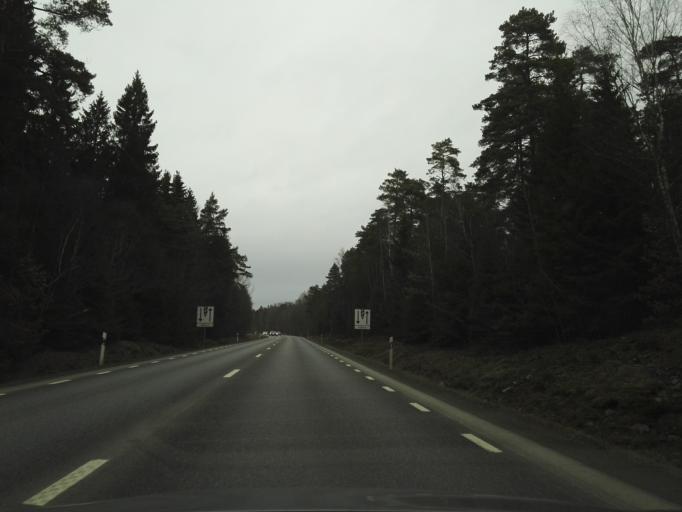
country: SE
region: Kronoberg
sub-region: Vaxjo Kommun
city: Vaexjoe
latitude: 56.8924
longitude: 14.8286
